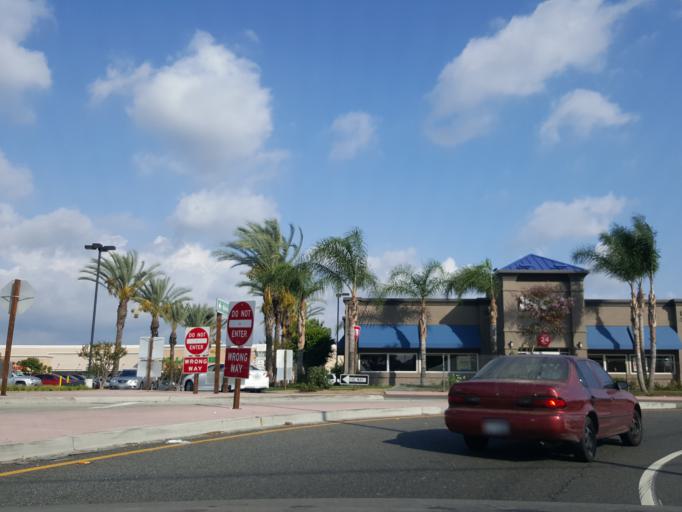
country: US
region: California
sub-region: Los Angeles County
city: Rosemead
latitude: 34.0740
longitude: -118.0728
